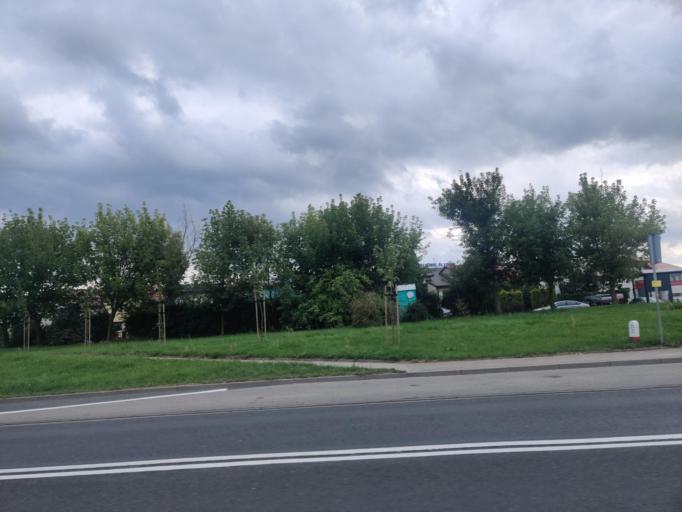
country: PL
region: Greater Poland Voivodeship
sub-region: Konin
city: Konin
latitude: 52.1995
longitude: 18.2900
